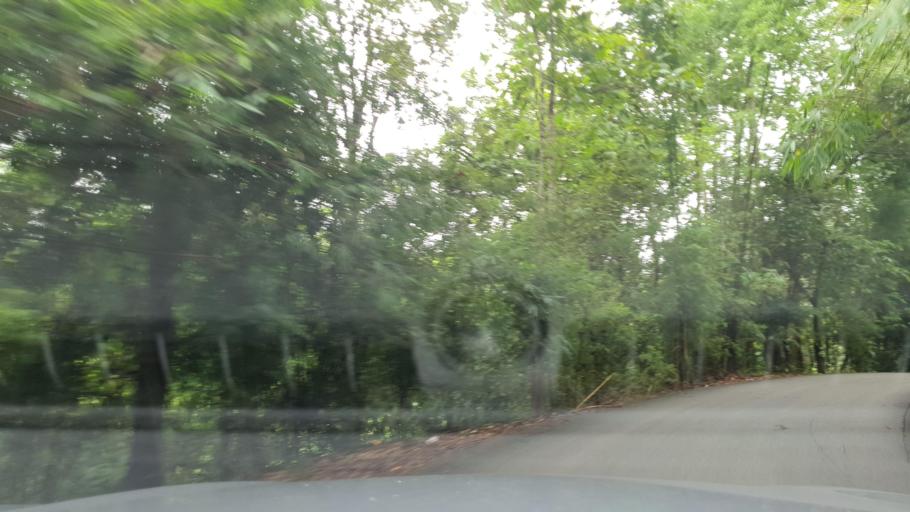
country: TH
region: Chiang Mai
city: Mae Taeng
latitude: 19.2082
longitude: 98.9295
